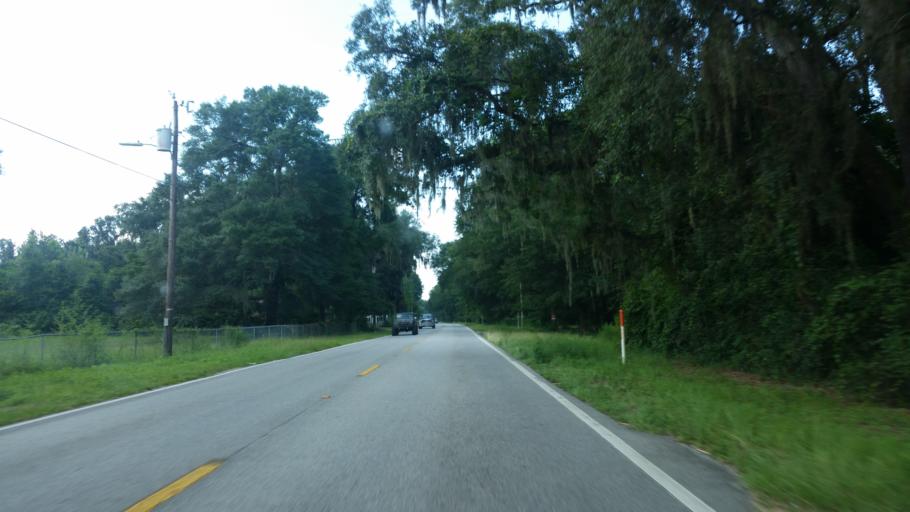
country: US
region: Florida
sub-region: Santa Rosa County
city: Bagdad
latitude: 30.5908
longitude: -87.0309
